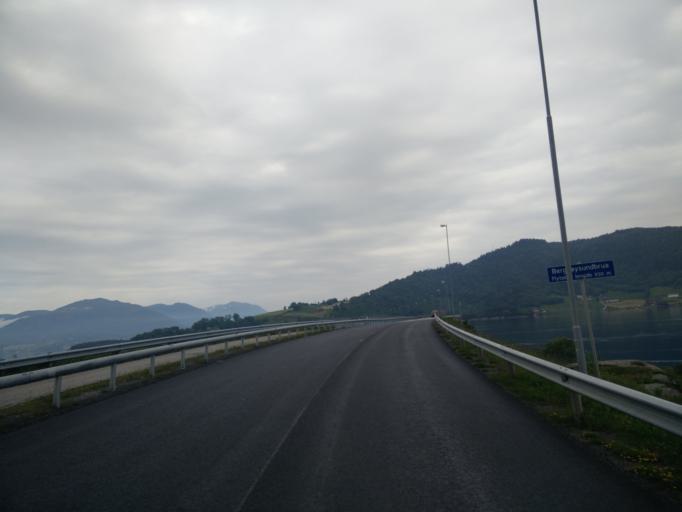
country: NO
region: More og Romsdal
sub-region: Kristiansund
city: Rensvik
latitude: 62.9900
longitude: 7.8818
